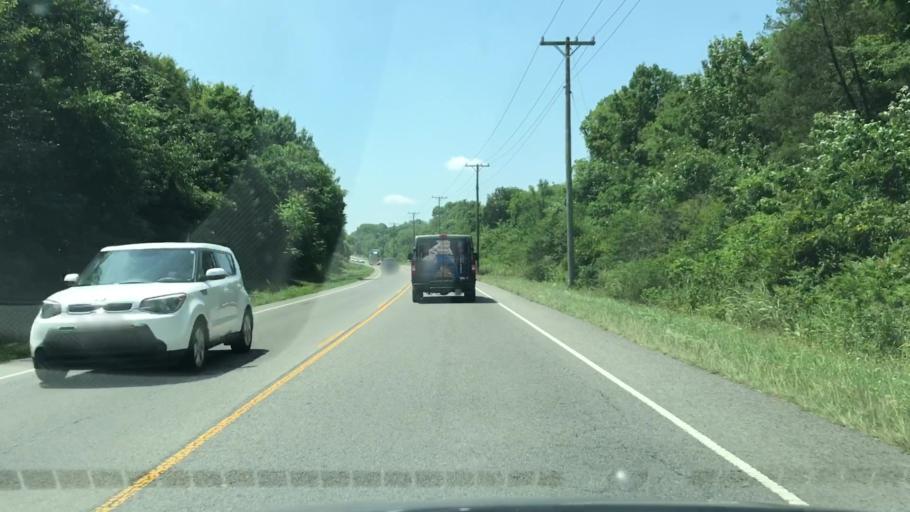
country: US
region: Tennessee
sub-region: Rutherford County
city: La Vergne
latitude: 35.9991
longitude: -86.6235
